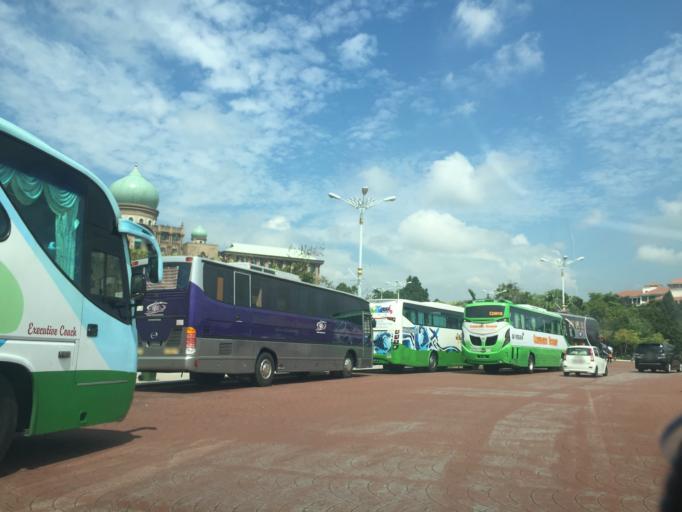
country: MY
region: Putrajaya
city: Putrajaya
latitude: 2.9359
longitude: 101.6908
